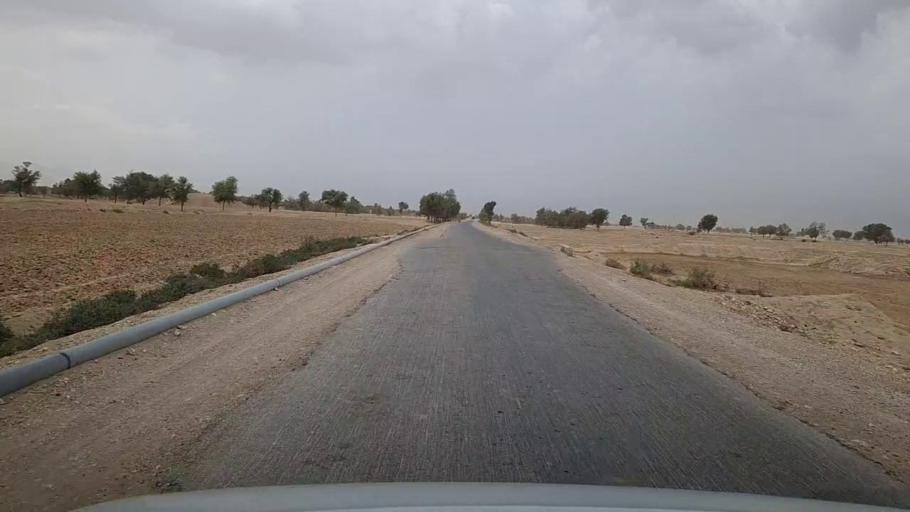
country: PK
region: Sindh
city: Sehwan
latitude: 26.3296
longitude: 67.7248
